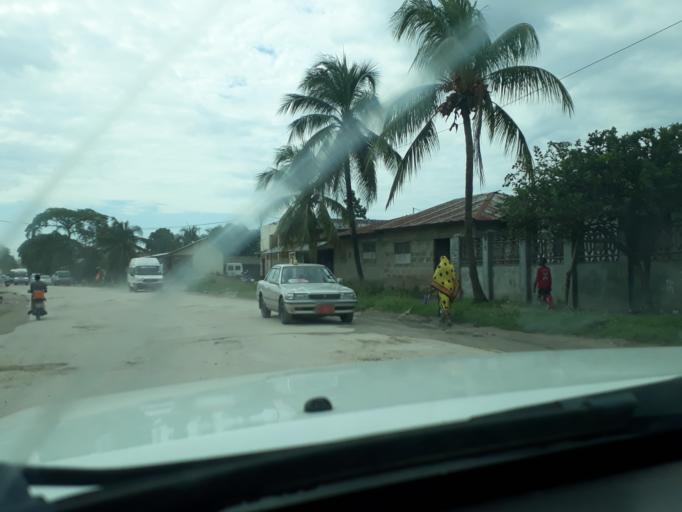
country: TZ
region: Zanzibar Central/South
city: Koani
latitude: -6.0835
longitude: 39.2227
